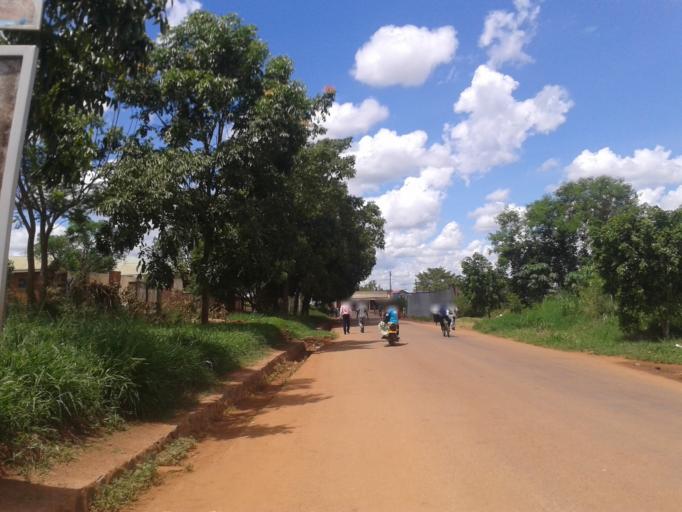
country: UG
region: Northern Region
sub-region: Gulu District
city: Gulu
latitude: 2.7763
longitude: 32.2980
